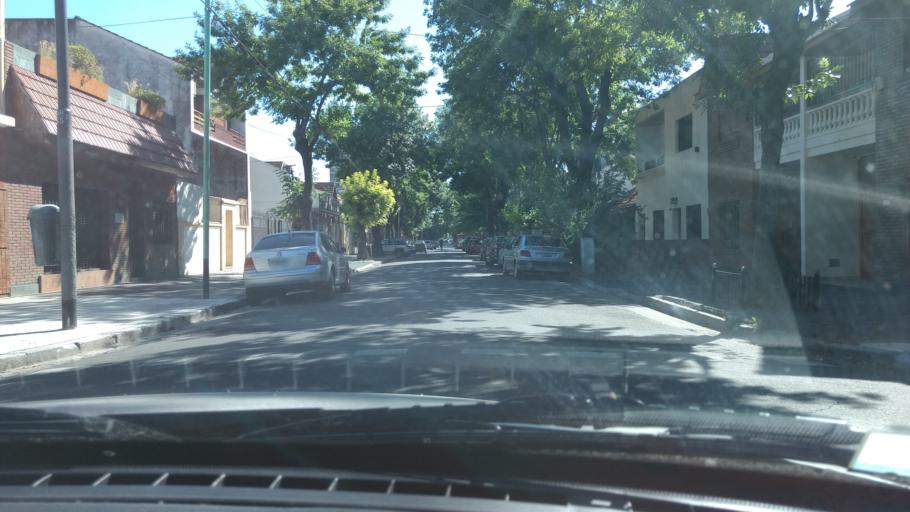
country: AR
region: Buenos Aires F.D.
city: Villa Santa Rita
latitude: -34.6109
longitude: -58.5110
